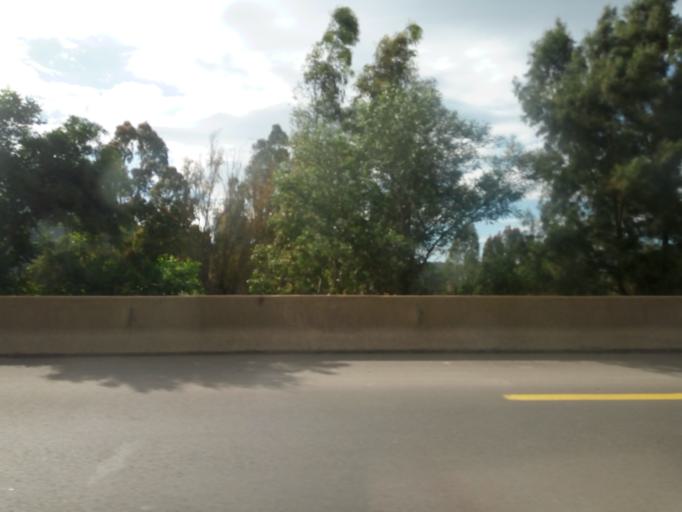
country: DZ
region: Tipaza
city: El Affroun
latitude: 36.4320
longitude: 2.5705
